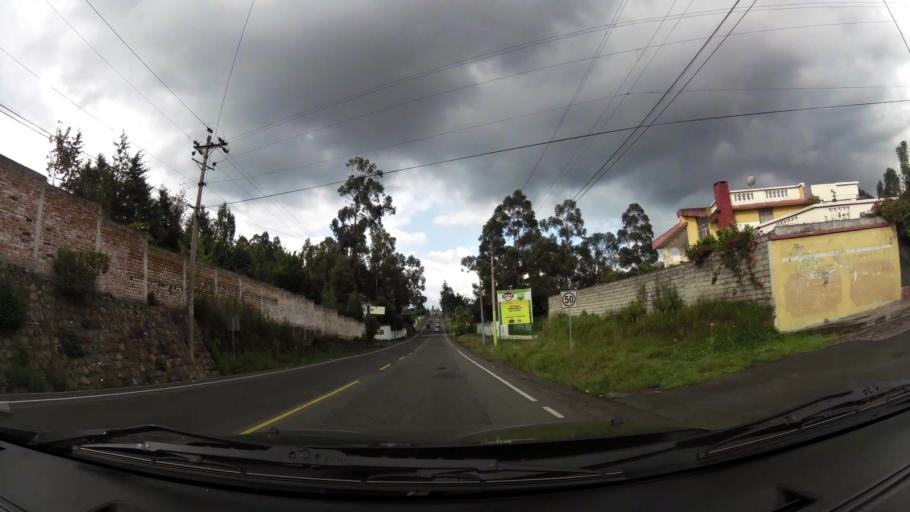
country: EC
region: Pichincha
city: Sangolqui
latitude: -0.3426
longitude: -78.4519
